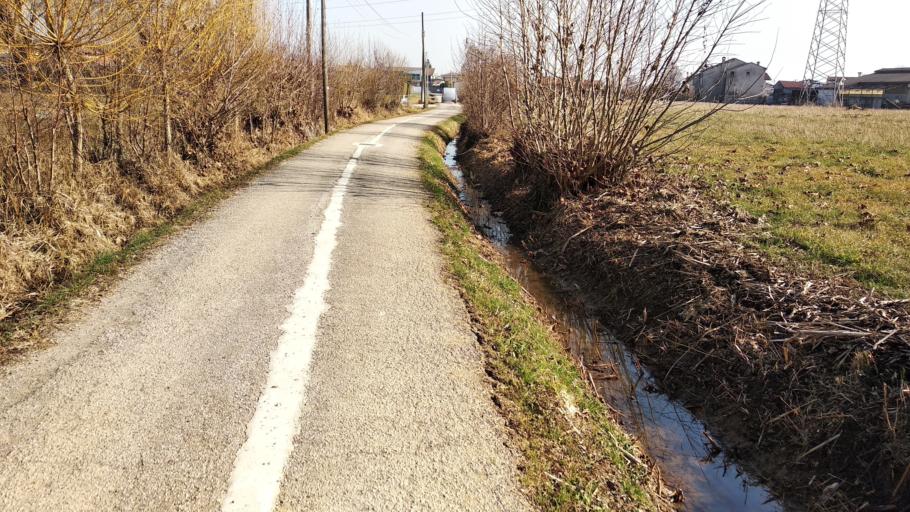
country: IT
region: Veneto
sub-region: Provincia di Vicenza
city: Crispi Cavour
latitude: 45.5879
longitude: 11.5139
